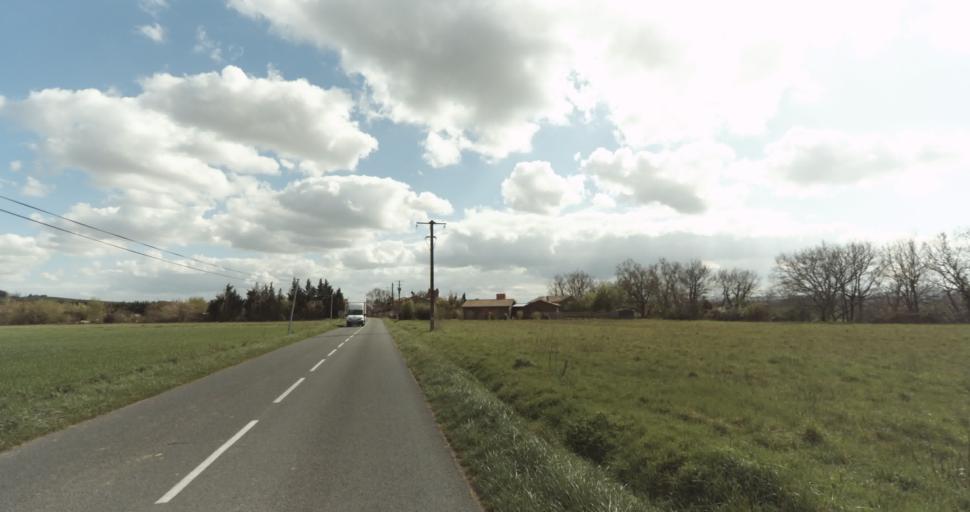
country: FR
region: Midi-Pyrenees
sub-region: Departement de la Haute-Garonne
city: Auterive
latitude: 43.3845
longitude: 1.4595
